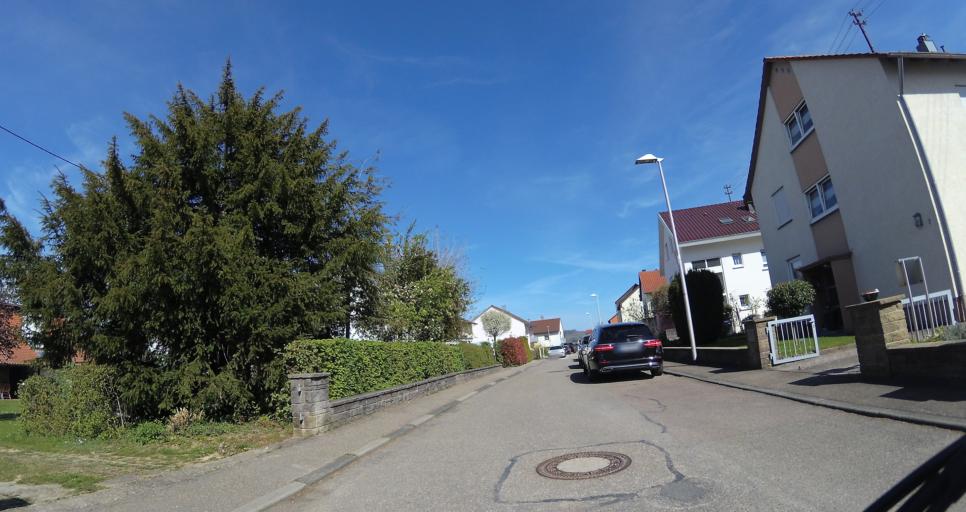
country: DE
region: Baden-Wuerttemberg
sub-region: Regierungsbezirk Stuttgart
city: Untereisesheim
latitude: 49.1948
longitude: 9.1979
